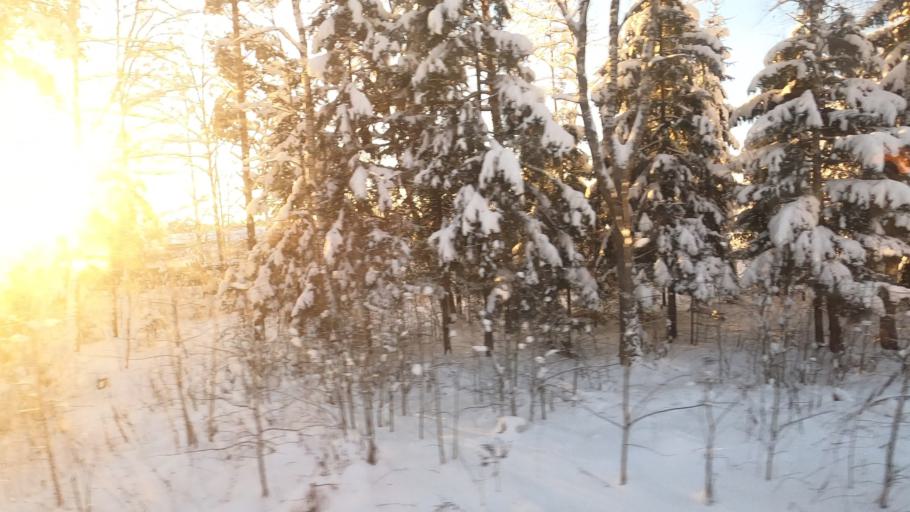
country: RU
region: Moskovskaya
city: Novo-Nikol'skoye
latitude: 56.5847
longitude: 37.5670
